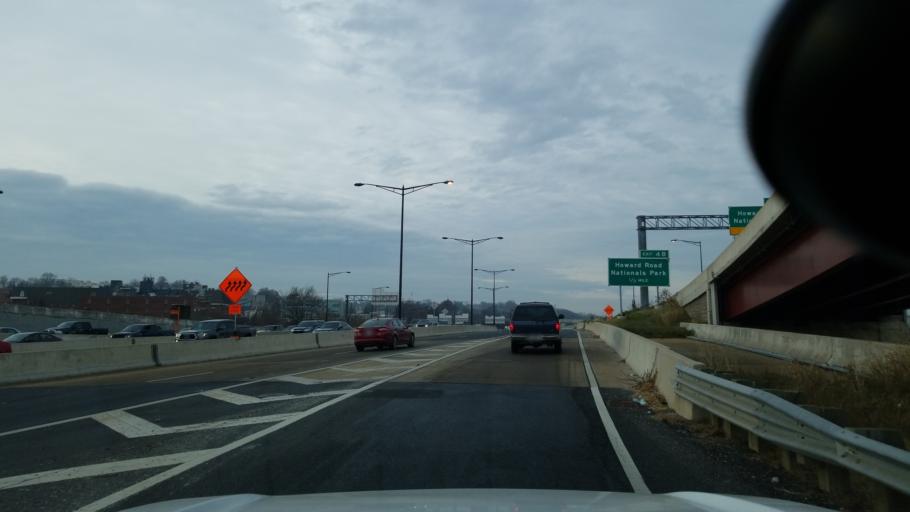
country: US
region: Maryland
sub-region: Prince George's County
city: Hillcrest Heights
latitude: 38.8688
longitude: -76.9895
